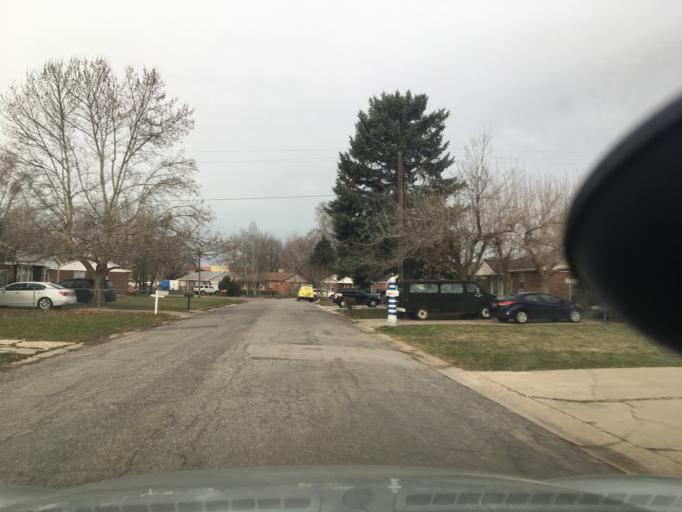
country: US
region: Utah
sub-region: Davis County
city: Layton
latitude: 41.0731
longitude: -111.9708
